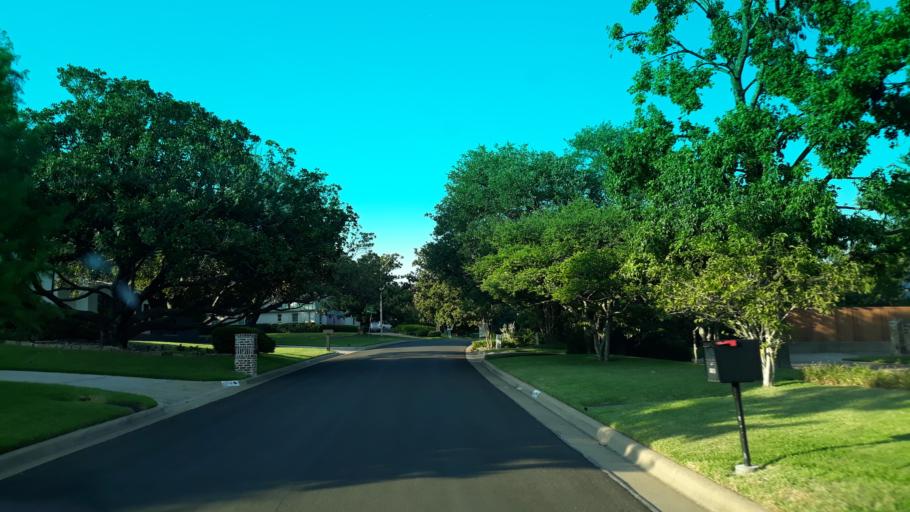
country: US
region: Texas
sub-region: Dallas County
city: Addison
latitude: 32.9456
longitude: -96.7913
